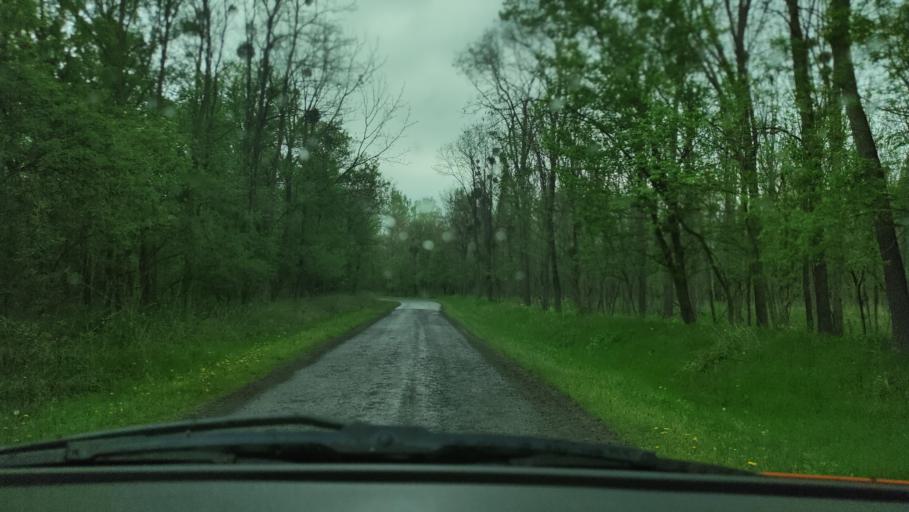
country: HU
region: Baranya
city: Mohacs
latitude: 45.9111
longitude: 18.7524
